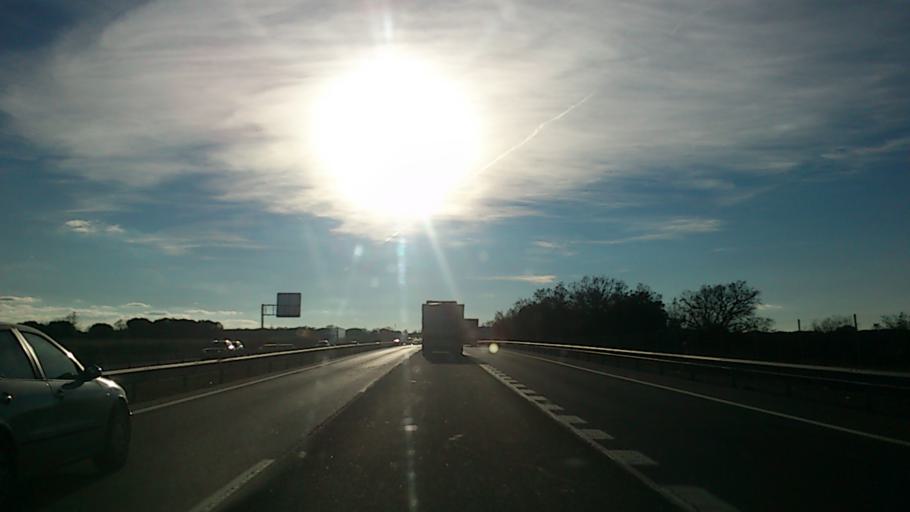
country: ES
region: Castille-La Mancha
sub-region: Provincia de Guadalajara
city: Almadrones
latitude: 40.9100
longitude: -2.7416
